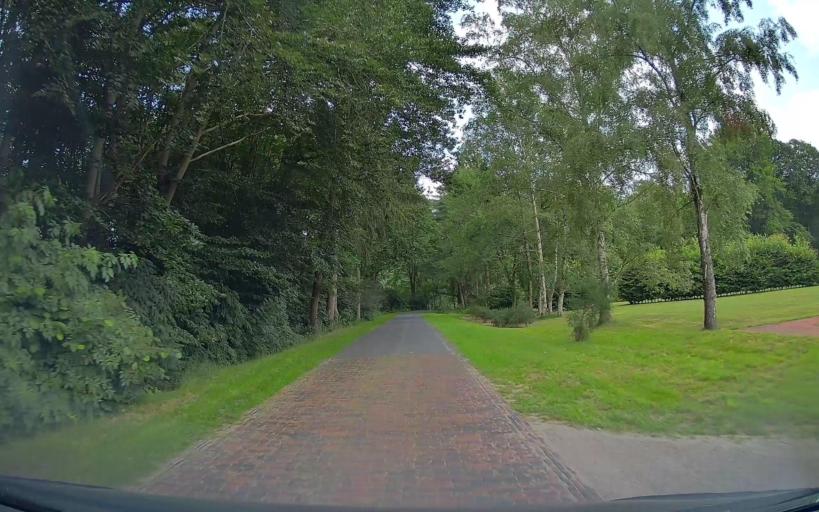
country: DE
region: Lower Saxony
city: Friesoythe
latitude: 52.9808
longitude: 7.8913
